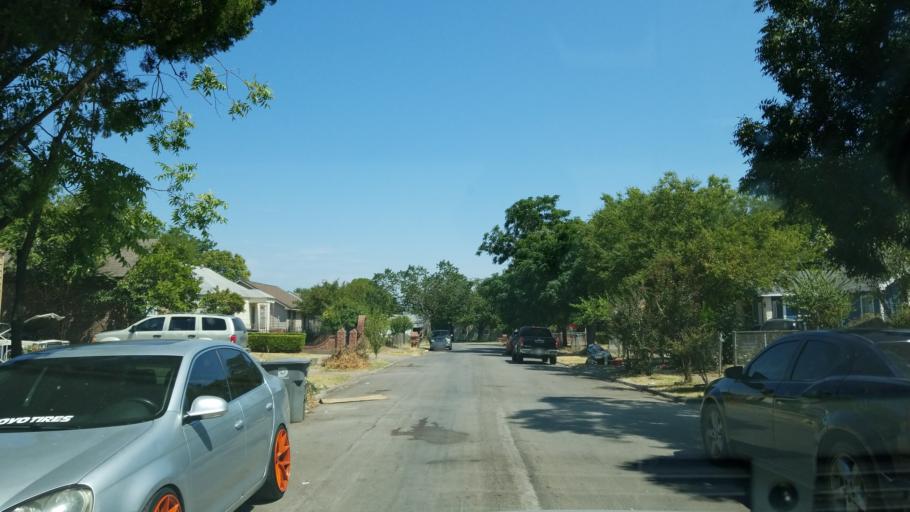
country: US
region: Texas
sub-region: Dallas County
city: Cockrell Hill
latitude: 32.7464
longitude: -96.8842
